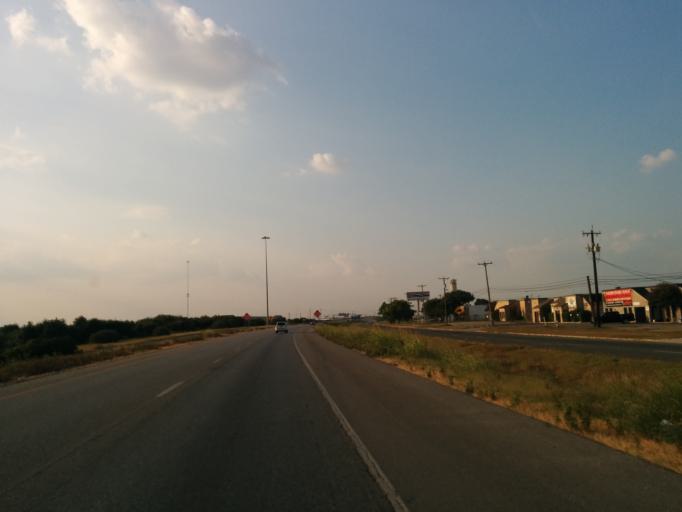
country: US
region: Texas
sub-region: Bexar County
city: Kirby
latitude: 29.4512
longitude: -98.4036
